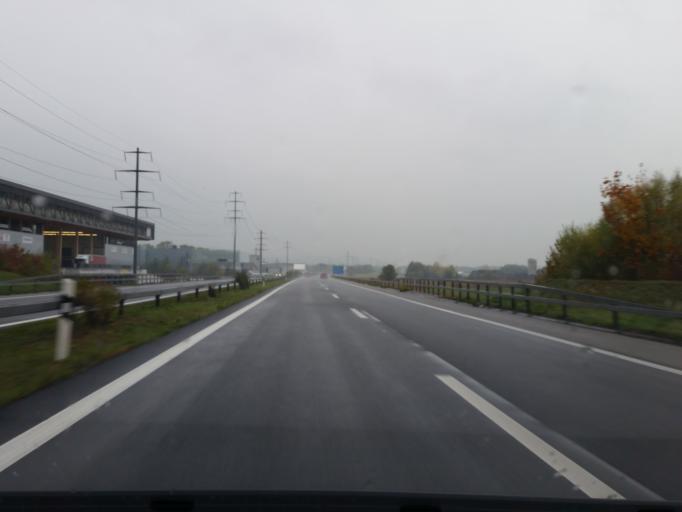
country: CH
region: Thurgau
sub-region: Frauenfeld District
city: Frauenfeld
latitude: 47.5768
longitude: 8.9204
